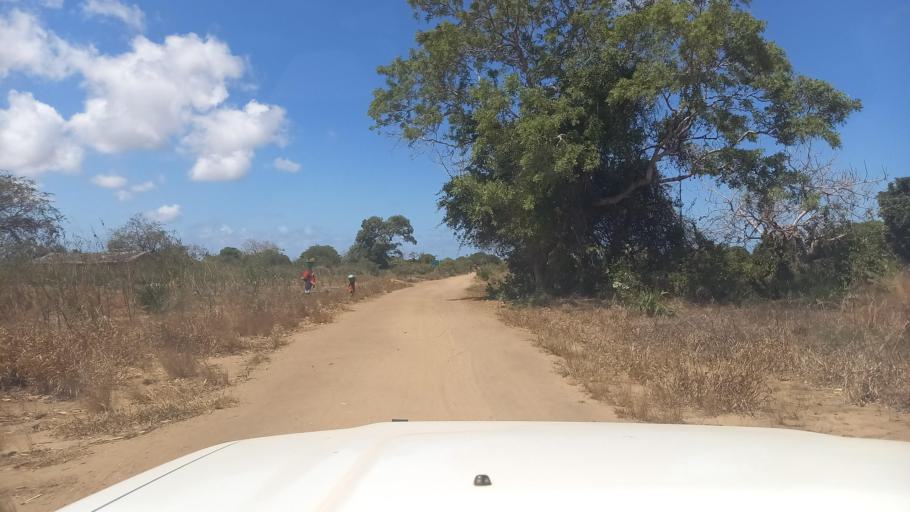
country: MZ
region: Cabo Delgado
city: Pemba
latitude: -13.4223
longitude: 40.5062
